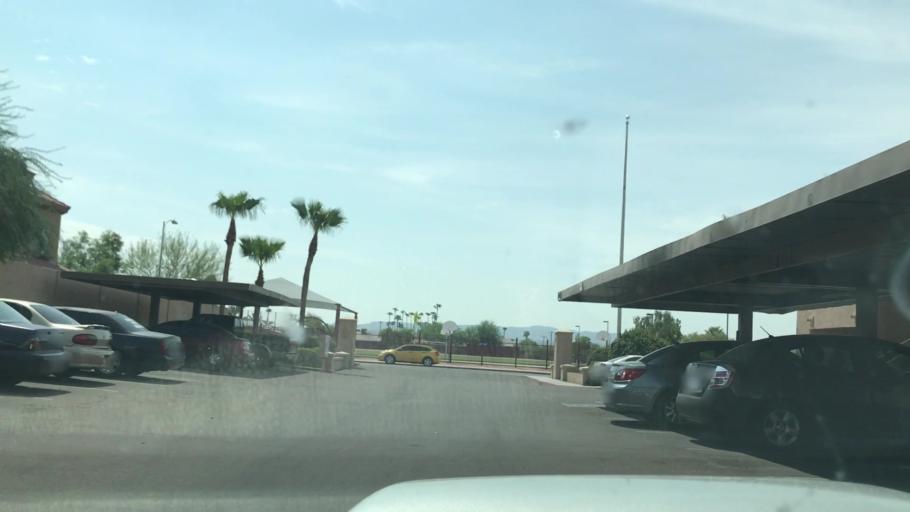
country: US
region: Arizona
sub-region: Maricopa County
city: Phoenix
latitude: 33.4554
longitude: -112.0190
